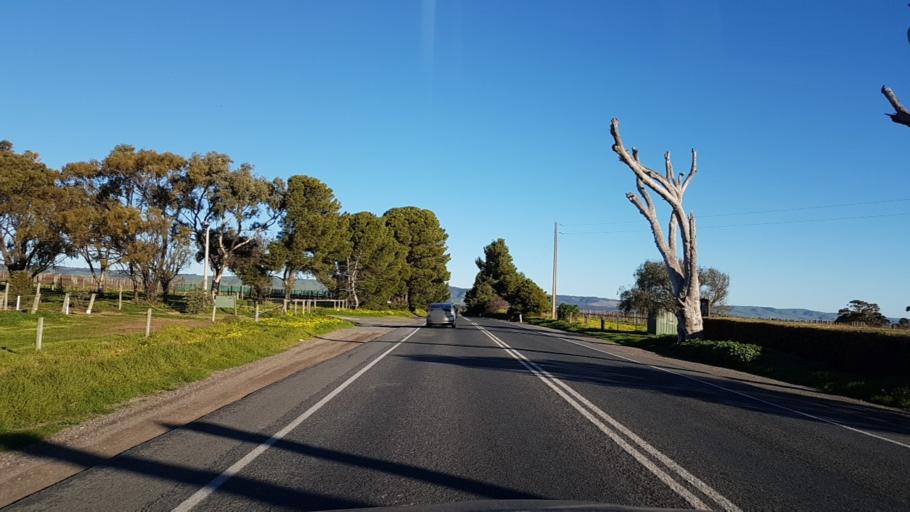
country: AU
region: South Australia
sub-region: Onkaparinga
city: Moana
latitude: -35.2374
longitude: 138.4936
